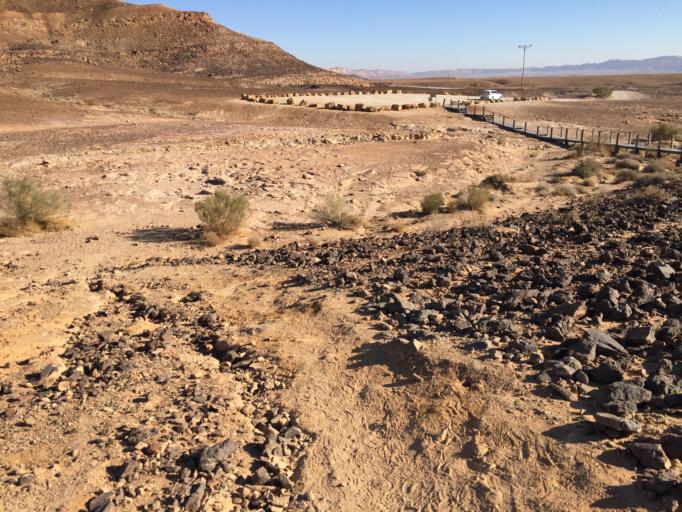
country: IL
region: Southern District
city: Mitzpe Ramon
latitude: 30.6167
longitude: 34.8395
